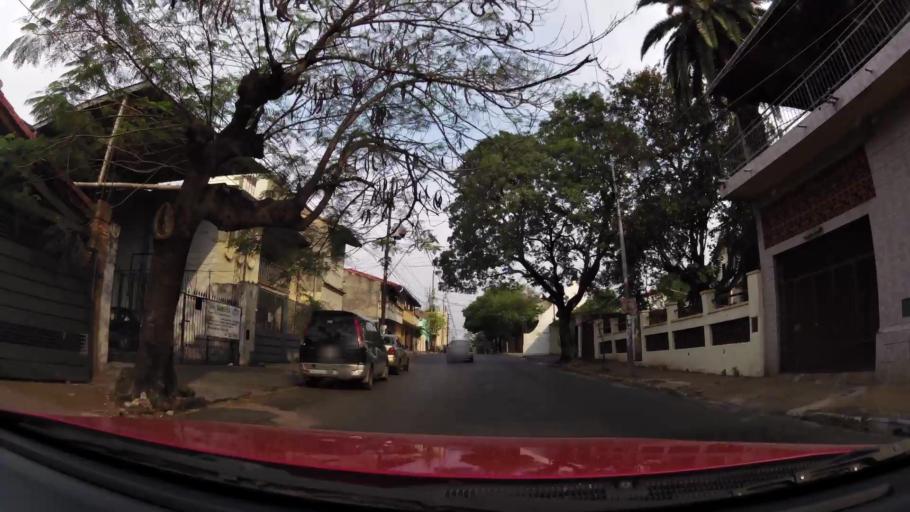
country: PY
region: Asuncion
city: Asuncion
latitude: -25.2983
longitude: -57.6288
